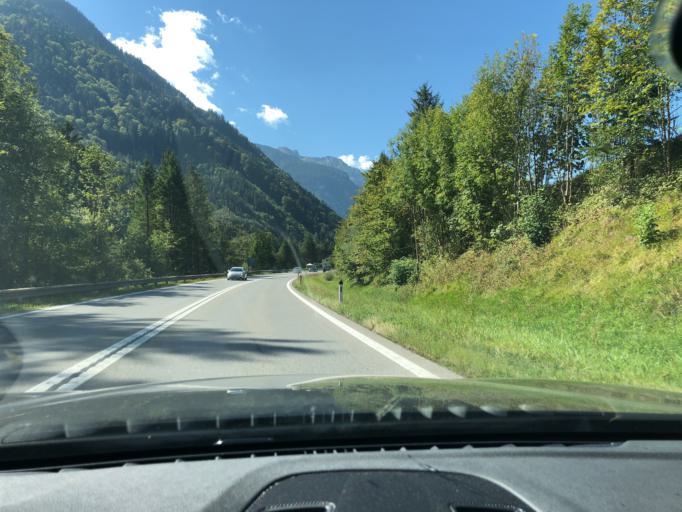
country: AT
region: Vorarlberg
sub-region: Politischer Bezirk Bludenz
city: Sankt Anton im Montafon
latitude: 47.1448
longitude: 9.8829
